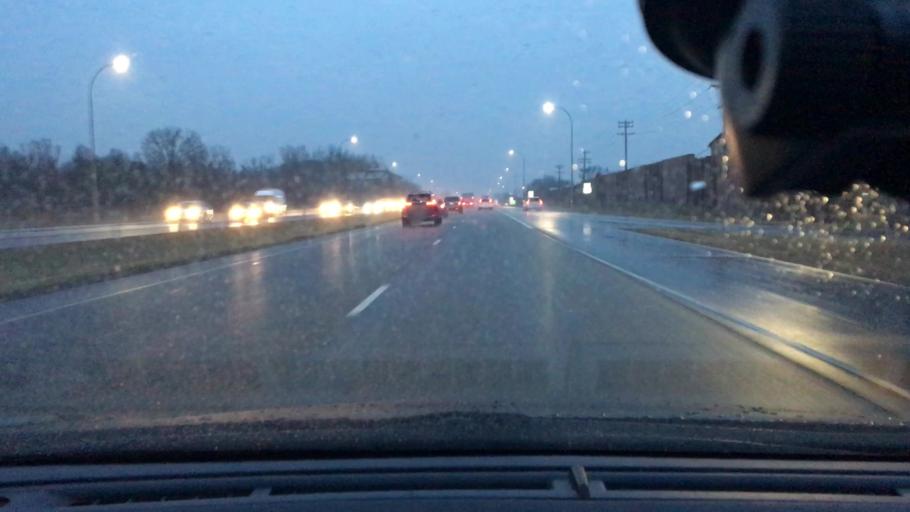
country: US
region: Minnesota
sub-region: Hennepin County
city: New Hope
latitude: 45.0361
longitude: -93.4006
